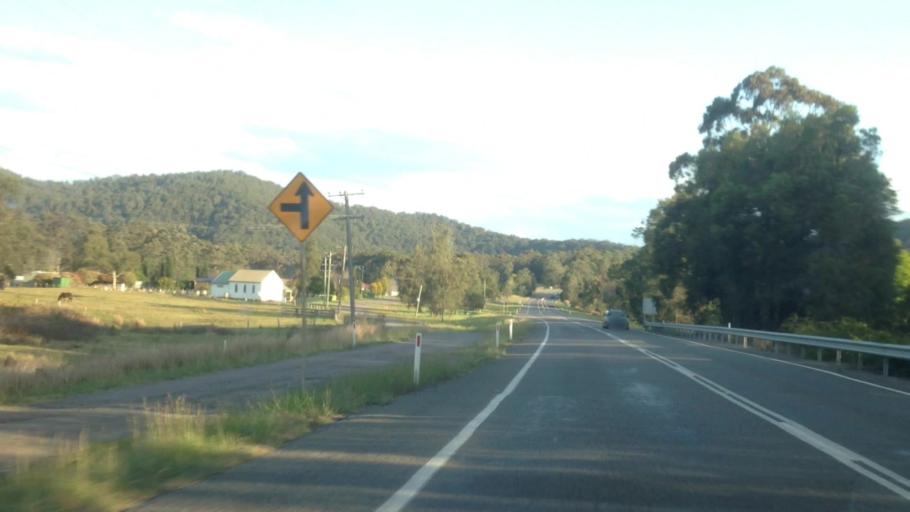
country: AU
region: New South Wales
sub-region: Lake Macquarie Shire
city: Holmesville
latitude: -32.9502
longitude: 151.4792
